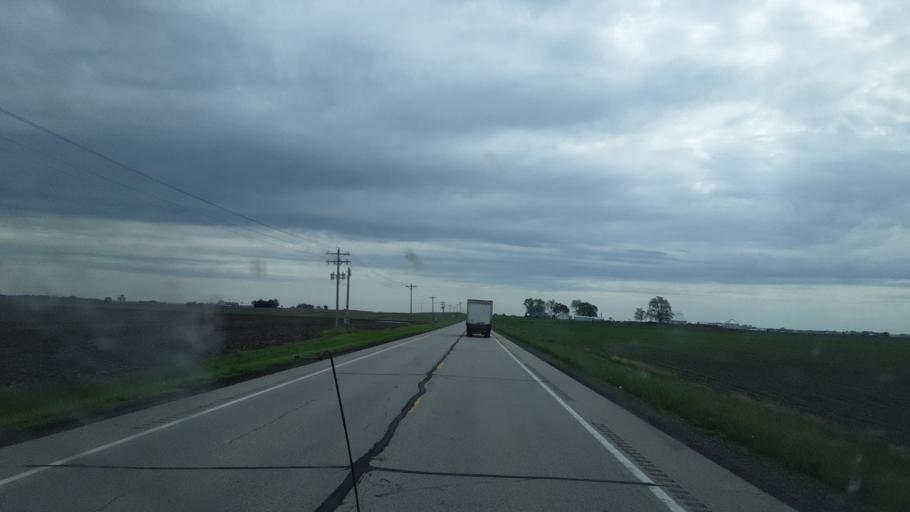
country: US
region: Illinois
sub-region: Mason County
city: Mason City
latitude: 40.3039
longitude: -89.7606
